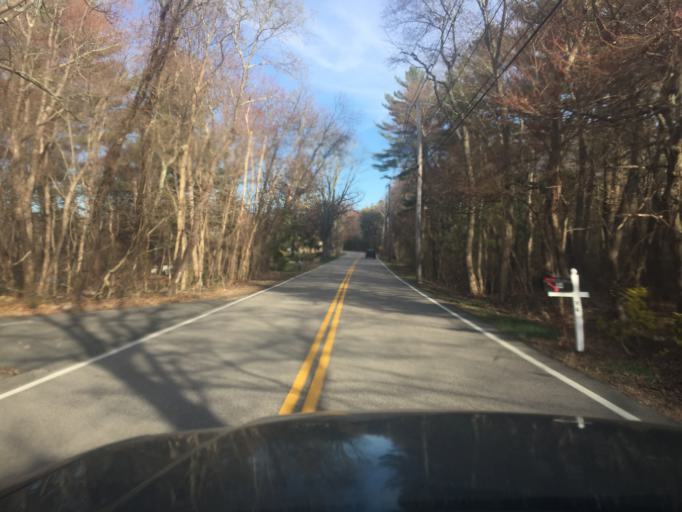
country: US
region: Massachusetts
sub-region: Worcester County
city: Milford
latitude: 42.1422
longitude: -71.4651
